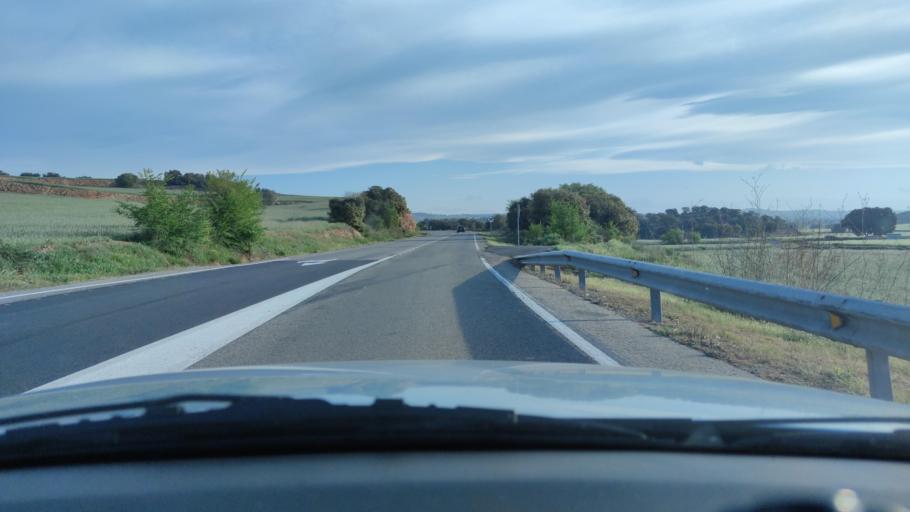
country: ES
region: Catalonia
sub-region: Provincia de Lleida
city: Agramunt
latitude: 41.8284
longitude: 1.0637
